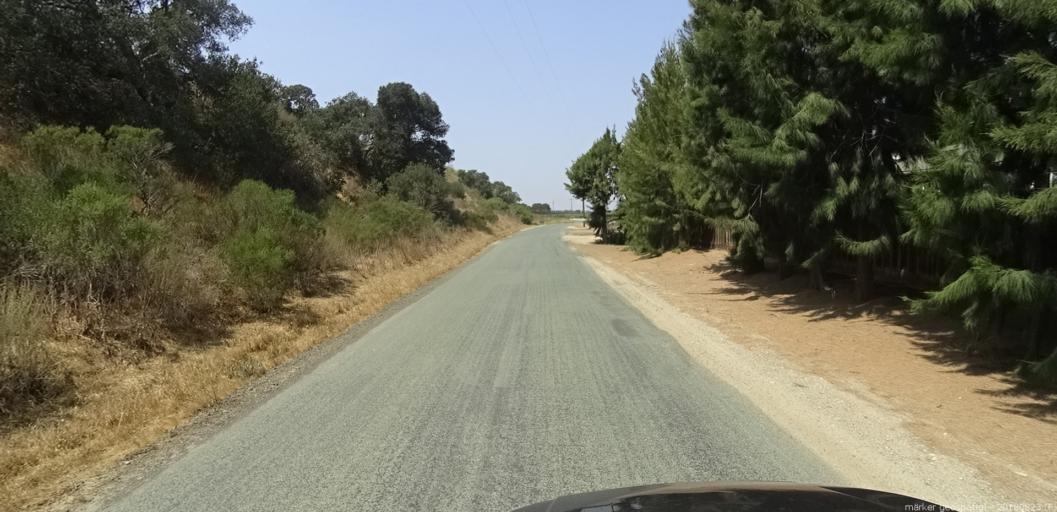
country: US
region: California
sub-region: Monterey County
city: Soledad
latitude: 36.3662
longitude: -121.3121
